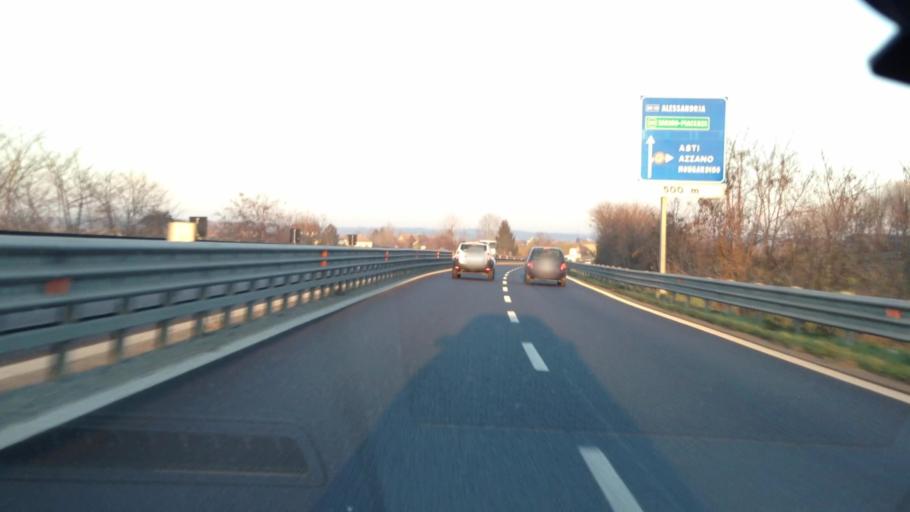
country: IT
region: Piedmont
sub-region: Provincia di Asti
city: Mongardino
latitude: 44.8731
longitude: 8.2100
